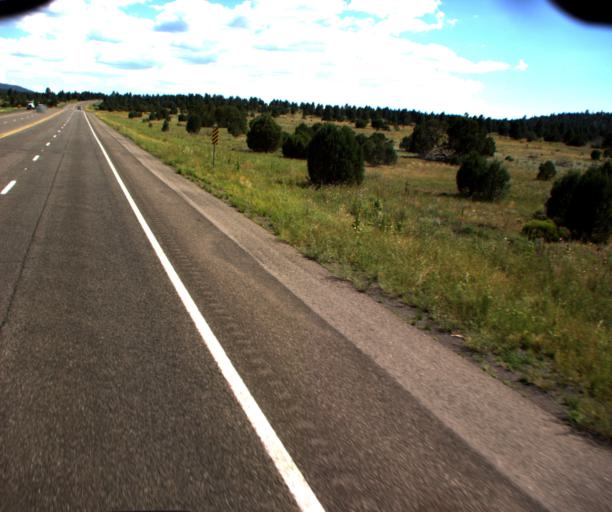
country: US
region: Arizona
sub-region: Coconino County
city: Williams
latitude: 35.3070
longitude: -112.1451
